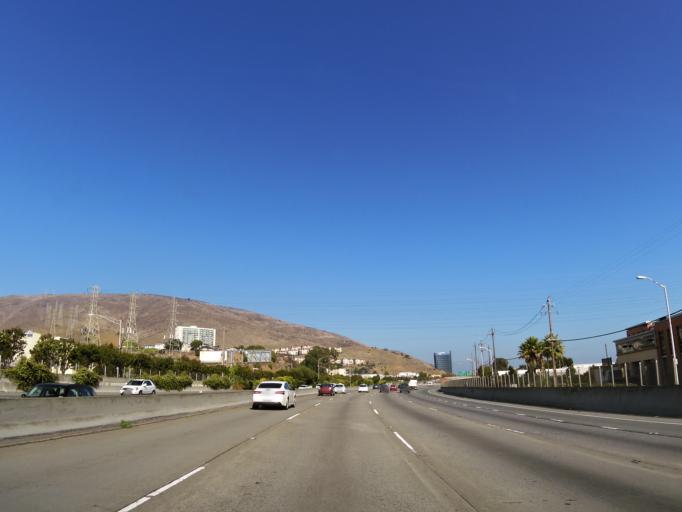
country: US
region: California
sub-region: San Mateo County
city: South San Francisco
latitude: 37.6589
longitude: -122.4051
